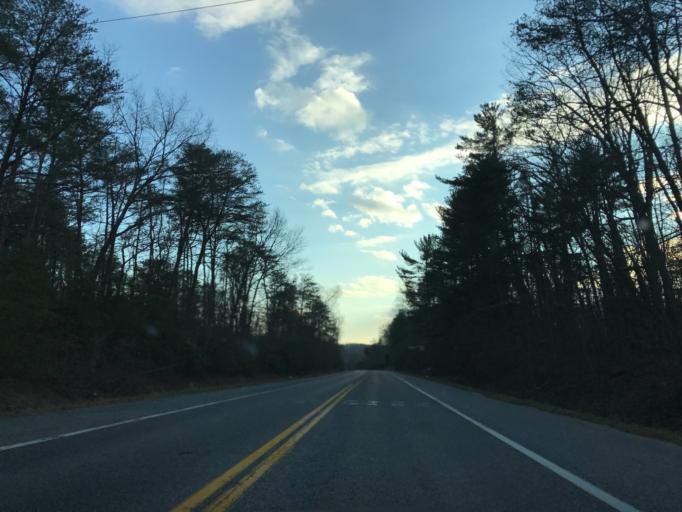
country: US
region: Maryland
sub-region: Cecil County
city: Charlestown
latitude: 39.5424
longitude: -75.9490
